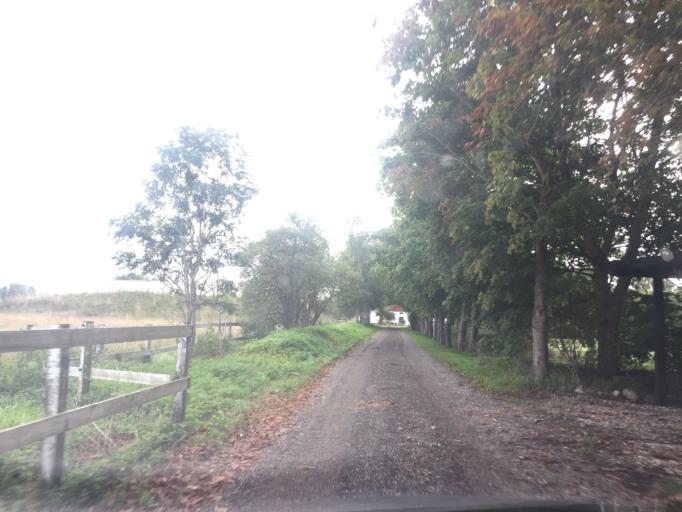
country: DK
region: Capital Region
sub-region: Hoje-Taastrup Kommune
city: Taastrup
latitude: 55.6715
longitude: 12.2781
